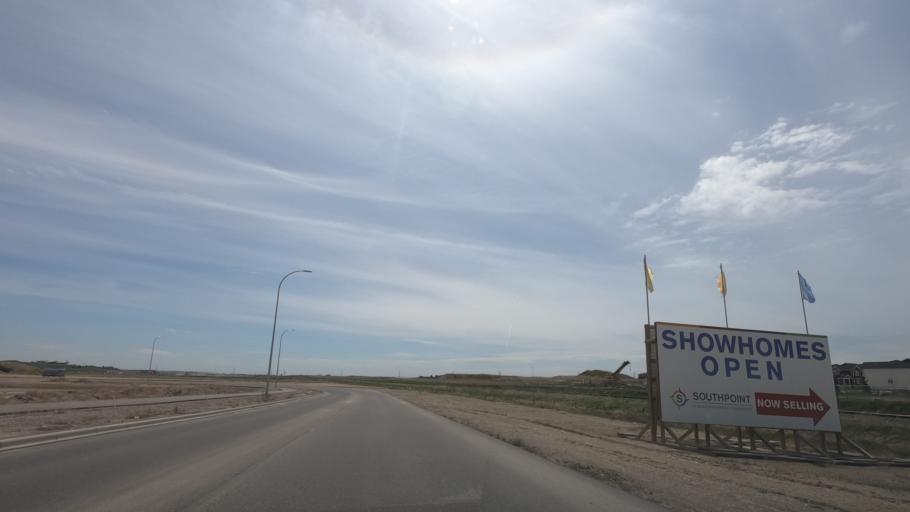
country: CA
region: Alberta
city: Airdrie
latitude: 51.2539
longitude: -114.0076
